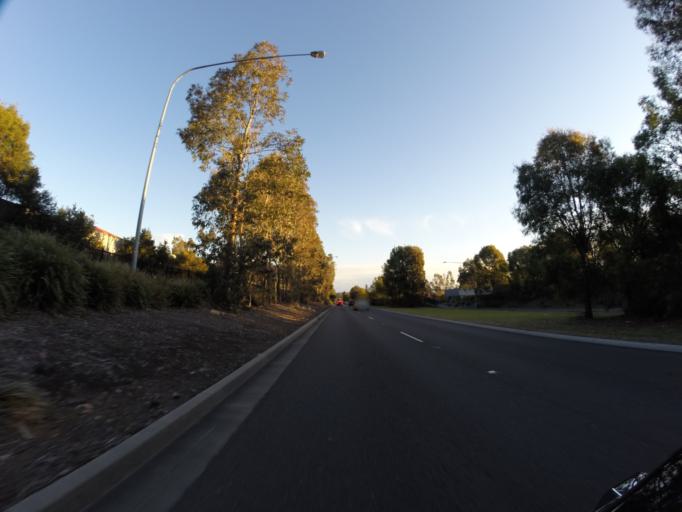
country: AU
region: New South Wales
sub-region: Fairfield
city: Cecil Park
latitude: -33.8914
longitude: 150.8592
